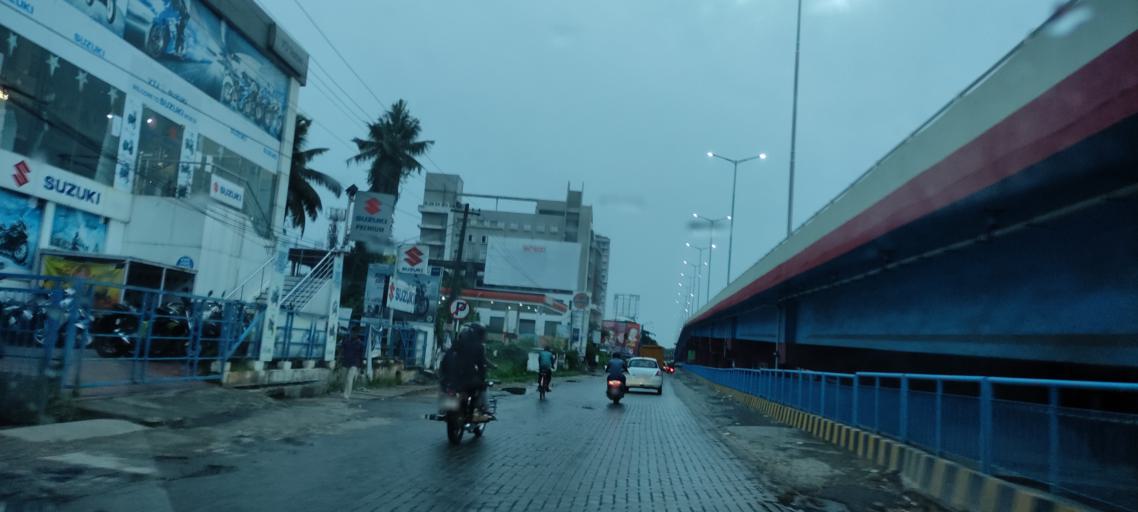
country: IN
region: Kerala
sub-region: Ernakulam
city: Cochin
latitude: 9.9387
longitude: 76.3182
